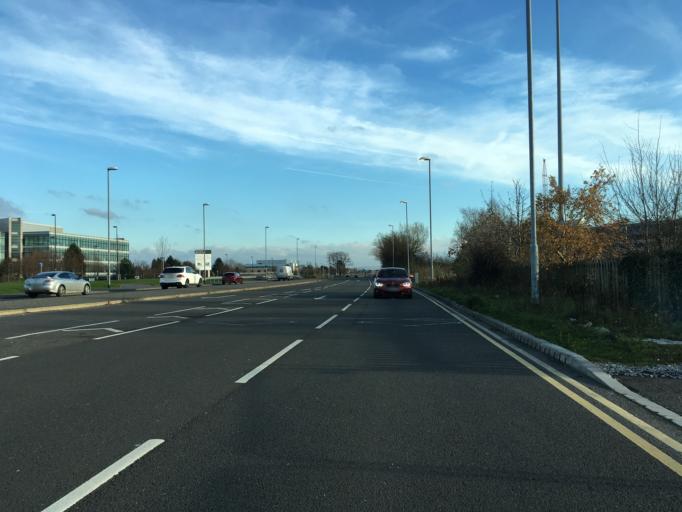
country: GB
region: England
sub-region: Manchester
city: Ringway
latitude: 53.3666
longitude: -2.2680
